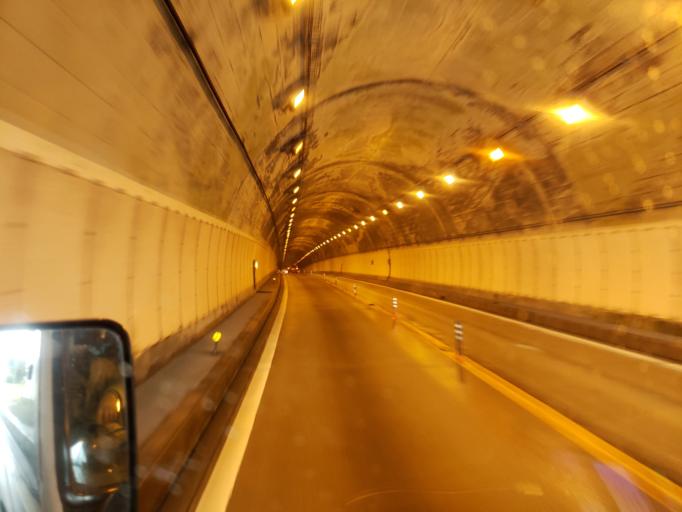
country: JP
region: Hyogo
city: Nishiwaki
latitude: 35.1388
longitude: 134.7900
